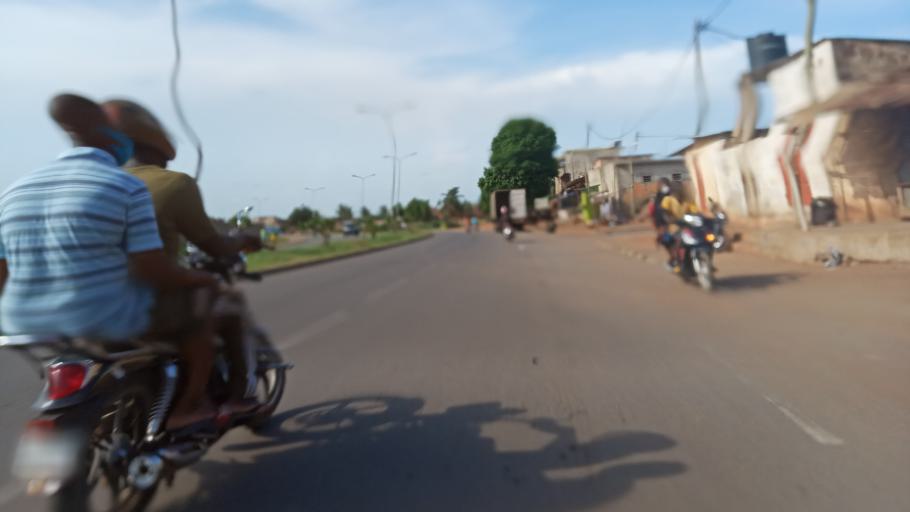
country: TG
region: Maritime
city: Lome
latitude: 6.1829
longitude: 1.2709
